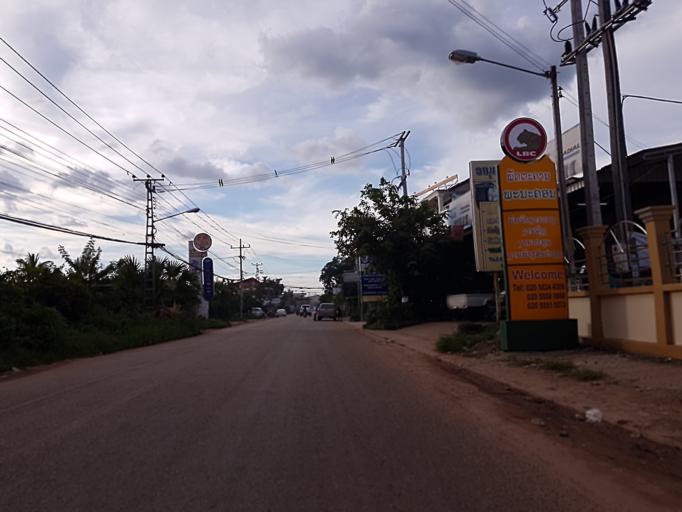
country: LA
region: Vientiane
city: Vientiane
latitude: 17.9786
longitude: 102.5880
